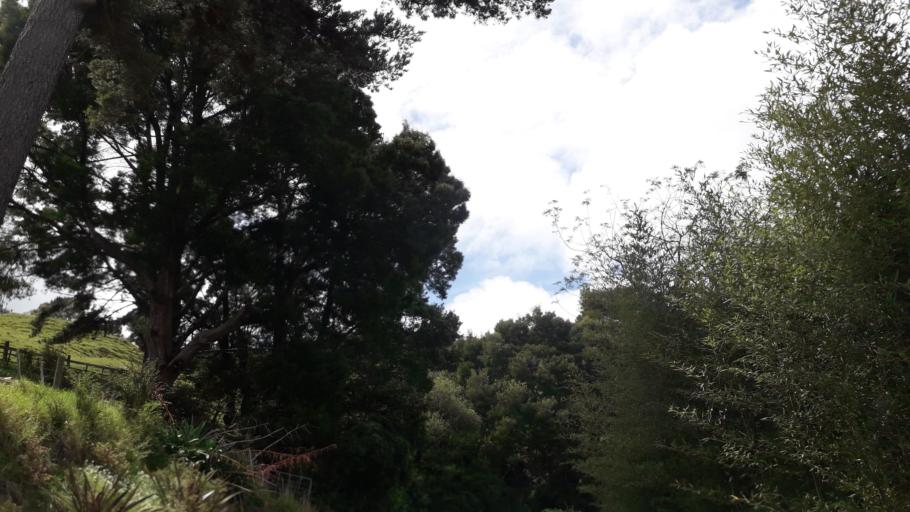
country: NZ
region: Northland
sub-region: Far North District
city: Taipa
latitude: -35.0942
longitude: 173.5352
